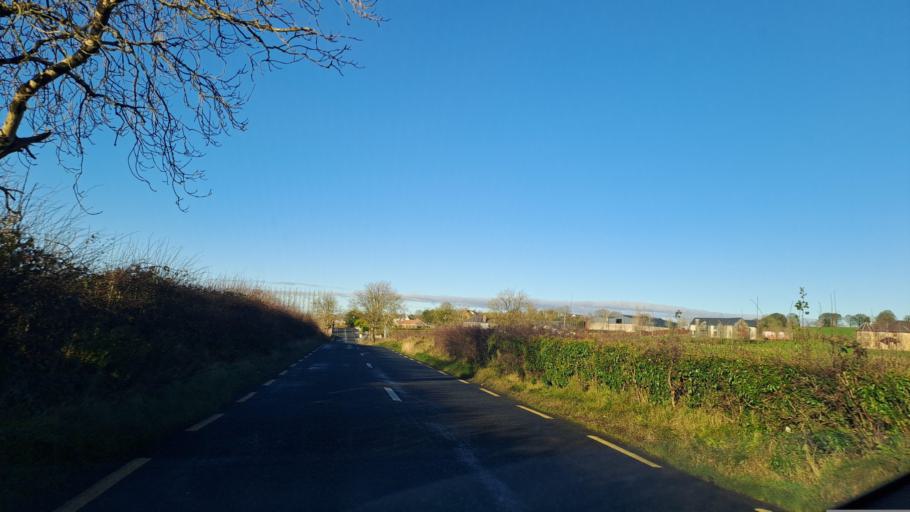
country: IE
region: Ulster
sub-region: An Cabhan
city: Mullagh
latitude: 53.8647
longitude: -6.9601
